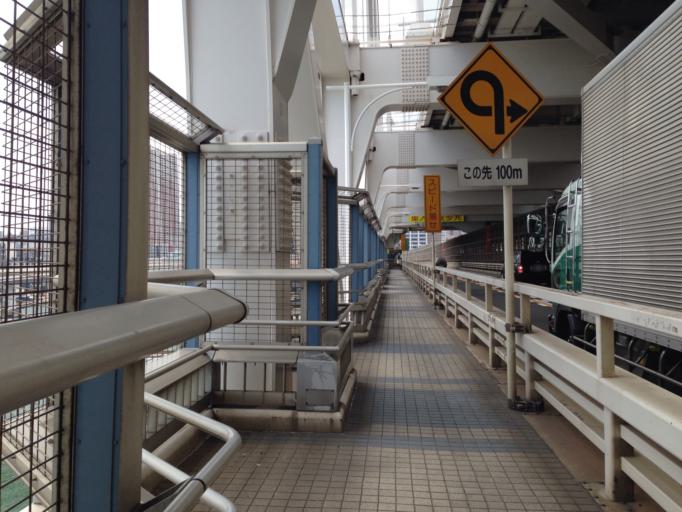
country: JP
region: Tokyo
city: Tokyo
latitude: 35.6373
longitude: 139.7601
